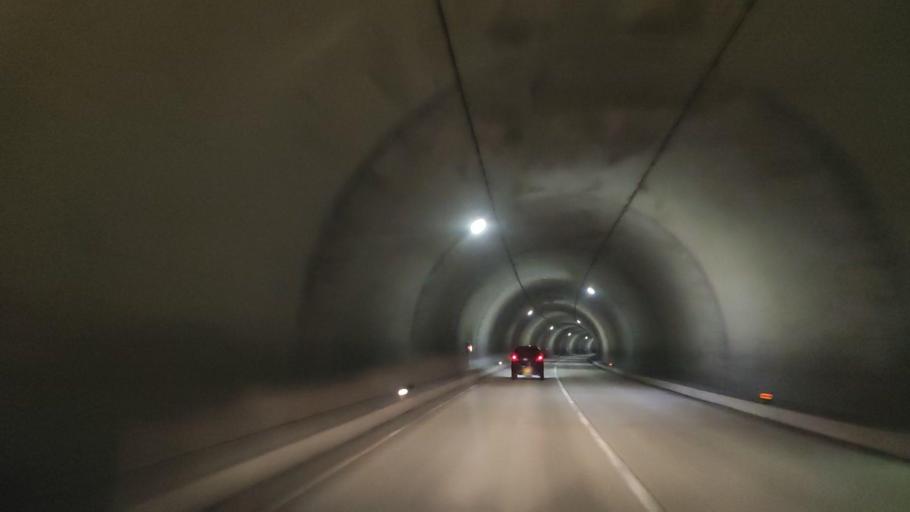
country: JP
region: Tottori
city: Kurayoshi
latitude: 35.4134
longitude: 133.8521
